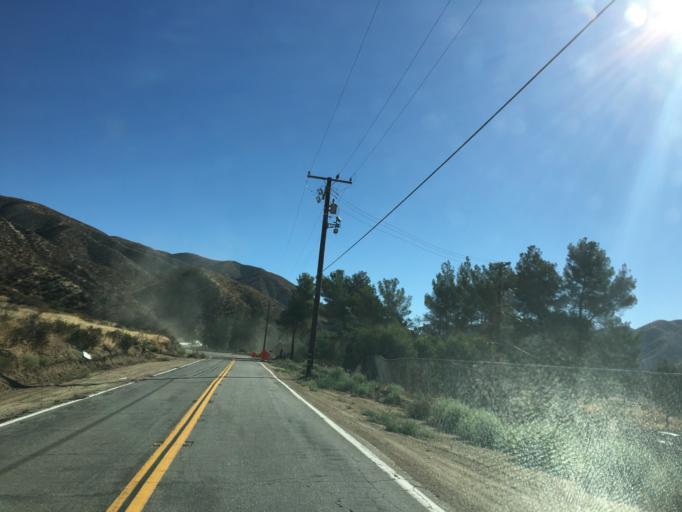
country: US
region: California
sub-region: Los Angeles County
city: Green Valley
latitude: 34.6517
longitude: -118.4822
